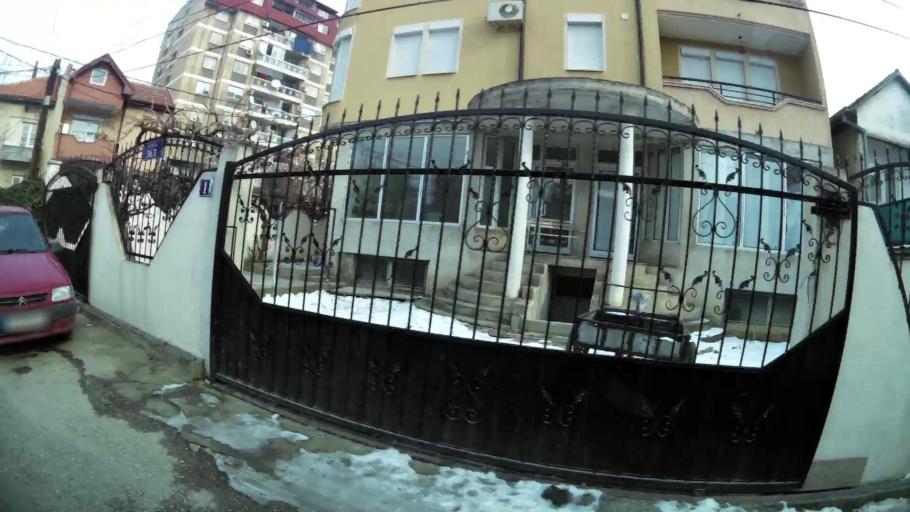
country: MK
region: Cair
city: Cair
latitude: 42.0124
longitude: 21.4369
